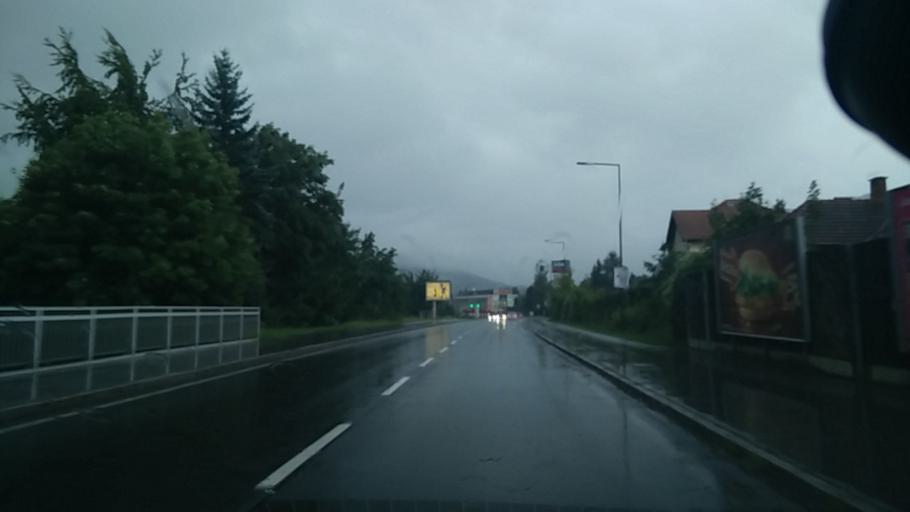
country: AT
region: Carinthia
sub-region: Villach Stadt
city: Villach
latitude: 46.6027
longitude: 13.8417
